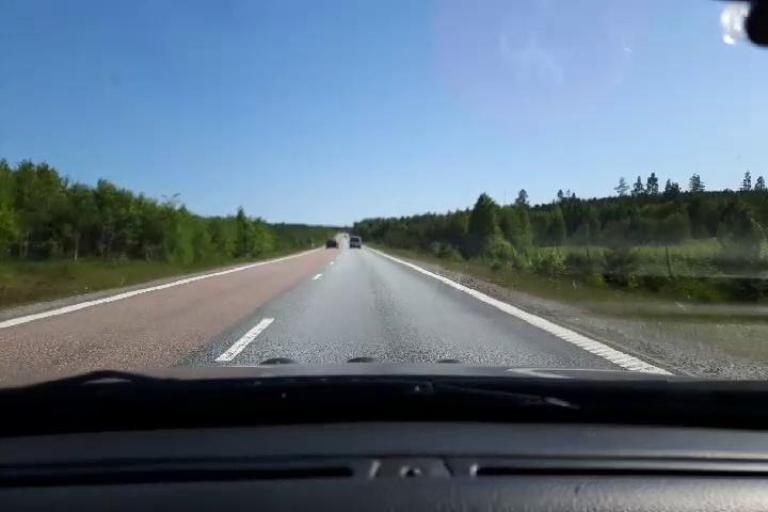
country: SE
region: Gaevleborg
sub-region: Hudiksvalls Kommun
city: Iggesund
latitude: 61.4826
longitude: 16.9854
